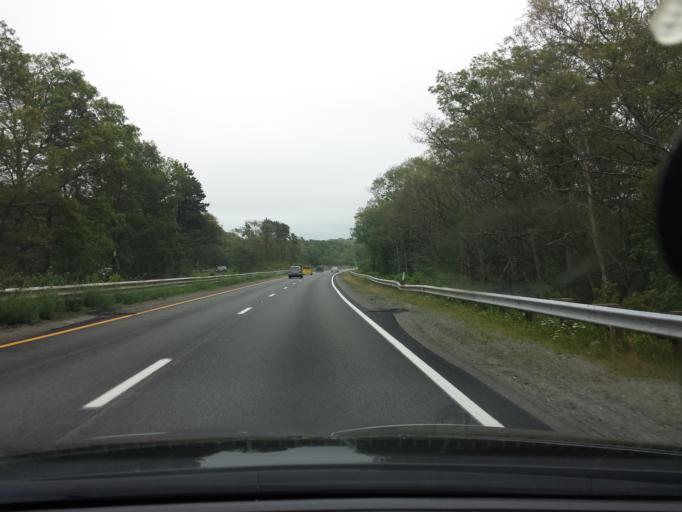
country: US
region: Massachusetts
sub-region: Barnstable County
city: East Sandwich
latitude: 41.7268
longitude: -70.4388
